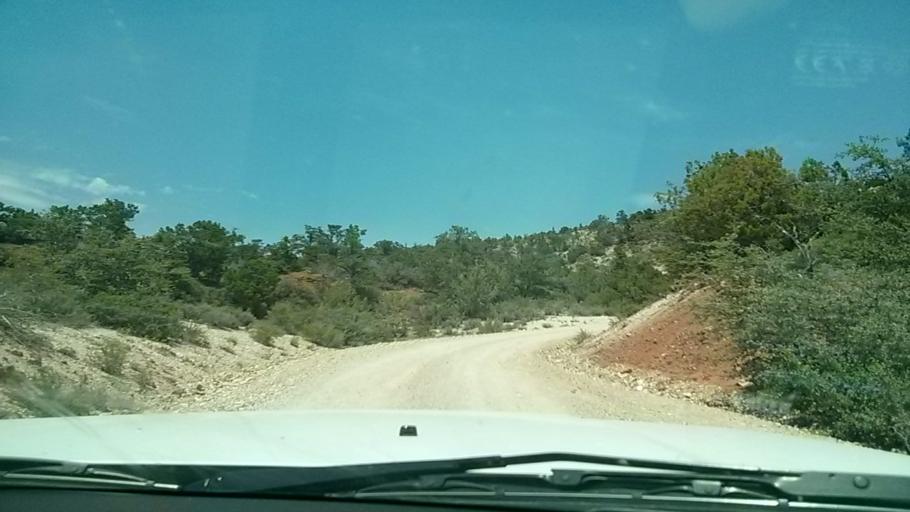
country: US
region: Utah
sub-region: Washington County
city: Toquerville
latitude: 37.2715
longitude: -113.4006
